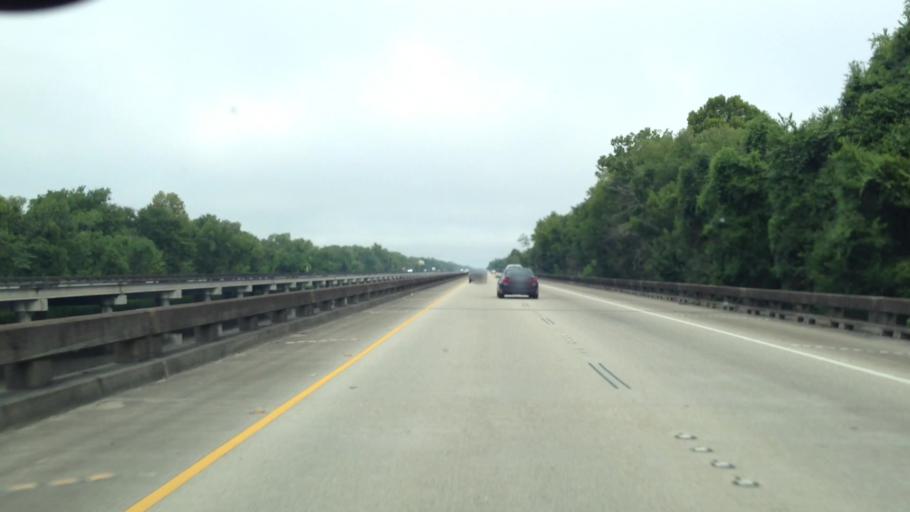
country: US
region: Louisiana
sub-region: Saint John the Baptist Parish
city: Montegut
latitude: 30.1086
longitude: -90.5154
